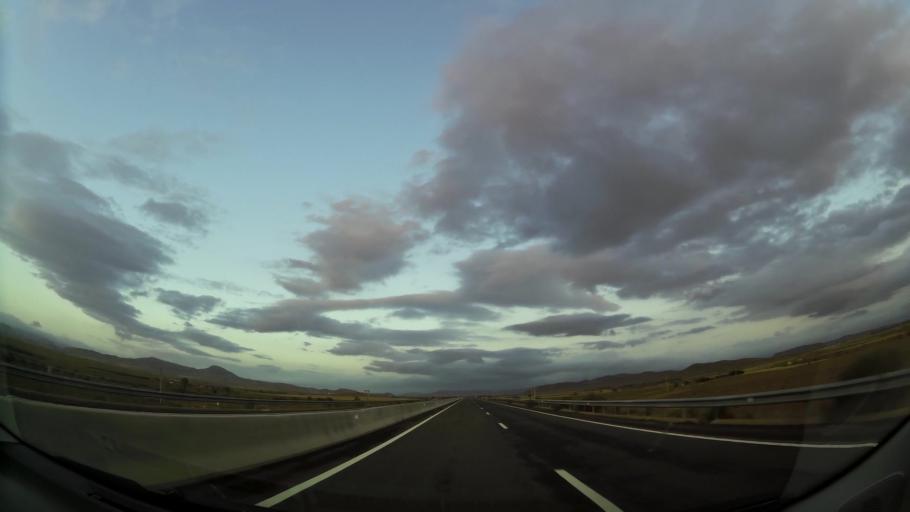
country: MA
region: Oriental
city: El Aioun
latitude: 34.6021
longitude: -2.7415
